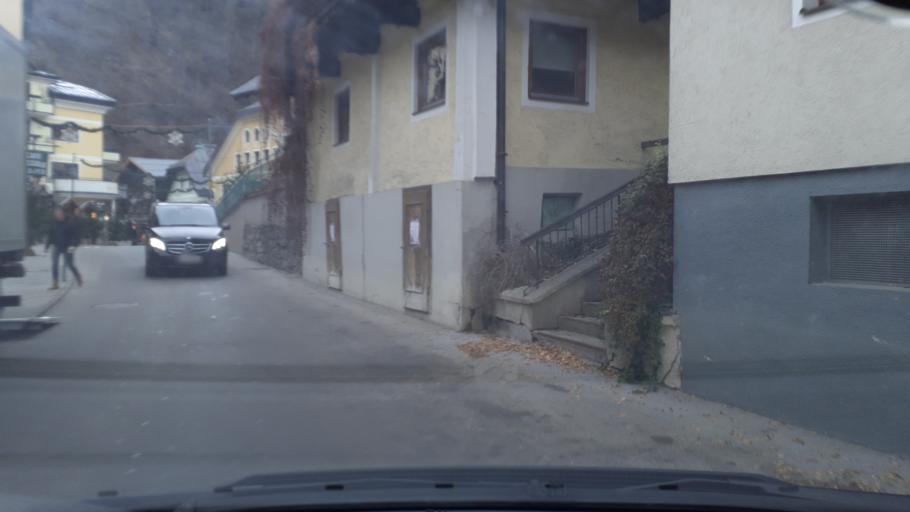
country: AT
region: Salzburg
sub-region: Politischer Bezirk Sankt Johann im Pongau
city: Huttschlag
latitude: 47.2367
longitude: 13.2008
